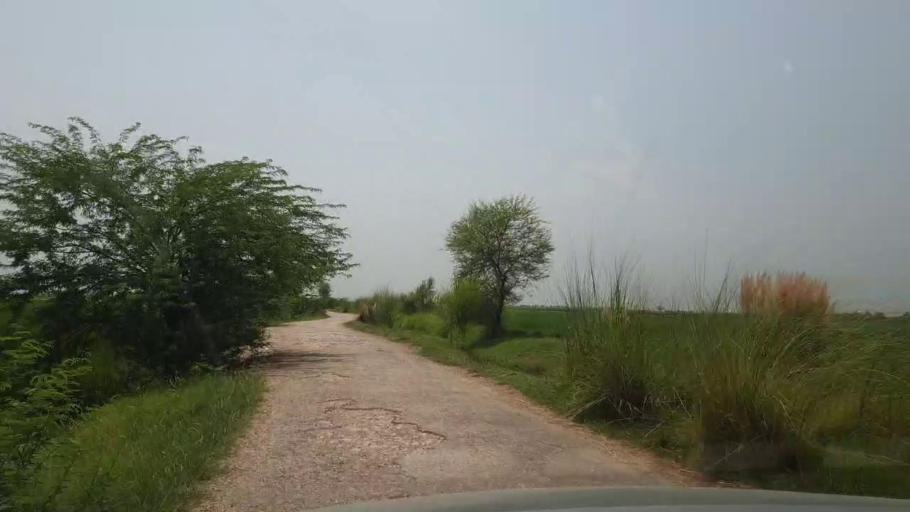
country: PK
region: Sindh
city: Garhi Yasin
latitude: 27.8721
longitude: 68.5009
